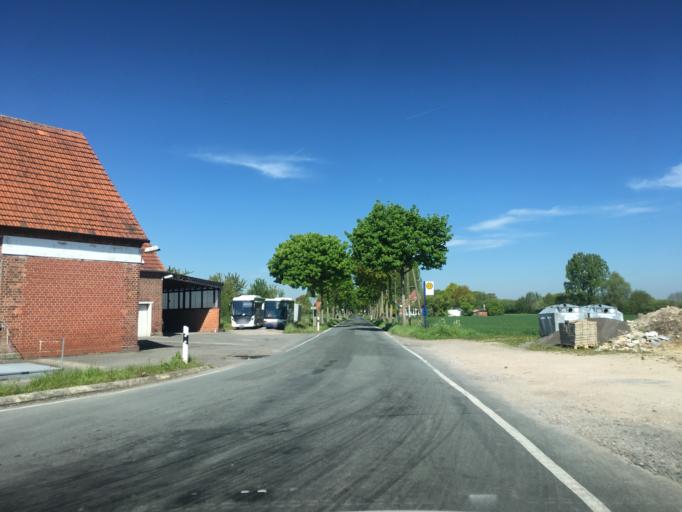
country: DE
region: North Rhine-Westphalia
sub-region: Regierungsbezirk Munster
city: Havixbeck
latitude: 52.0134
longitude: 7.4112
